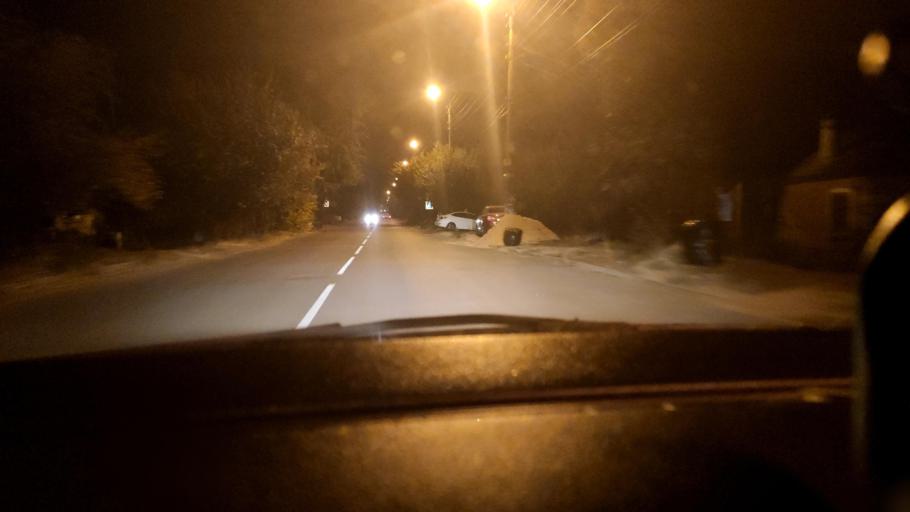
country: RU
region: Voronezj
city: Voronezh
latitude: 51.6422
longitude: 39.1707
